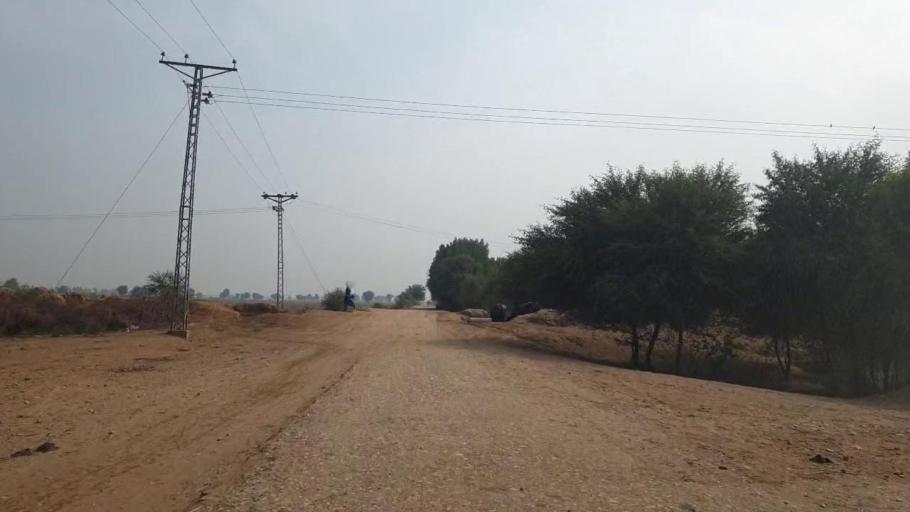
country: PK
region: Sindh
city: Sann
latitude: 26.0283
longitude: 68.1392
